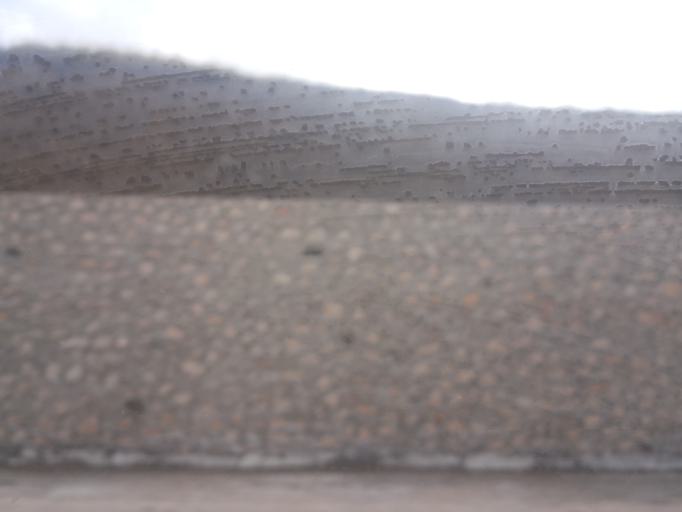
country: TR
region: Tokat
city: Bereketli
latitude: 40.5350
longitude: 37.3043
